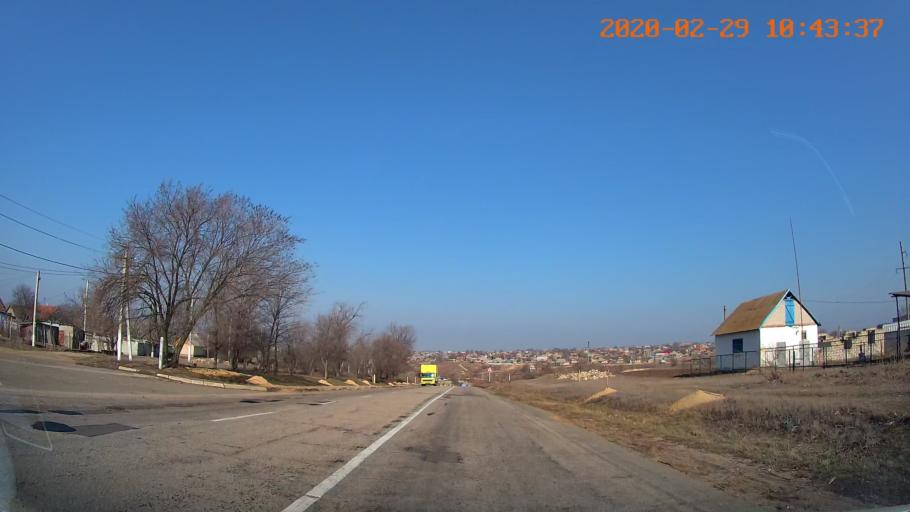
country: MD
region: Telenesti
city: Grigoriopol
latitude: 47.0634
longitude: 29.4025
